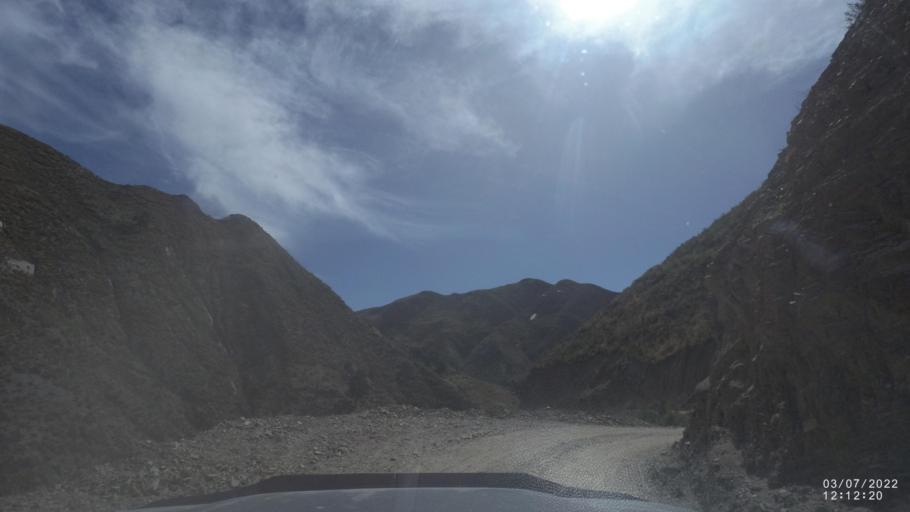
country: BO
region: Cochabamba
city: Irpa Irpa
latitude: -17.8388
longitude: -66.6129
